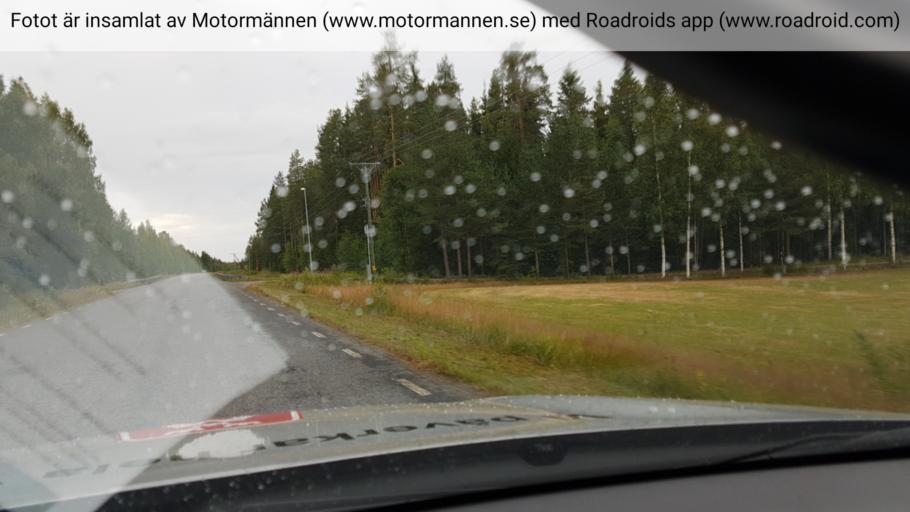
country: SE
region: Norrbotten
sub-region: Bodens Kommun
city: Boden
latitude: 65.8328
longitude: 21.5012
